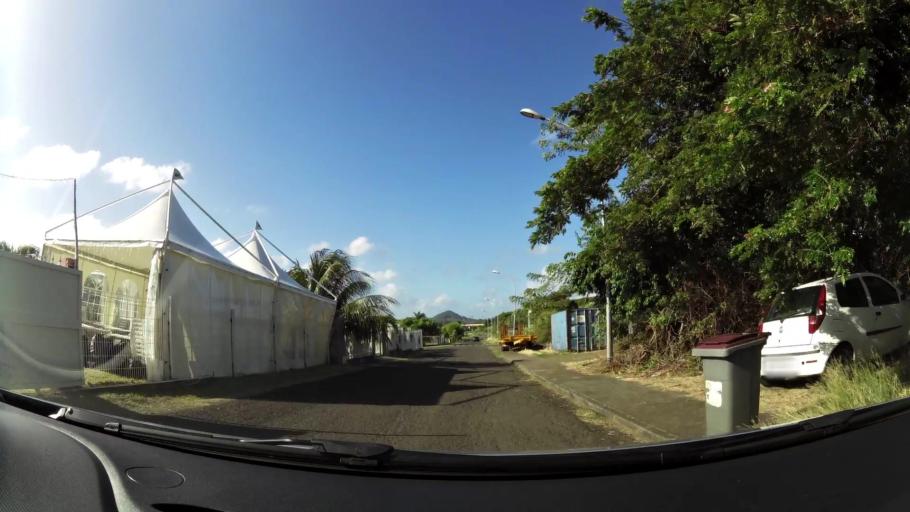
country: MQ
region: Martinique
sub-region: Martinique
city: Le Francois
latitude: 14.6226
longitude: -60.9021
